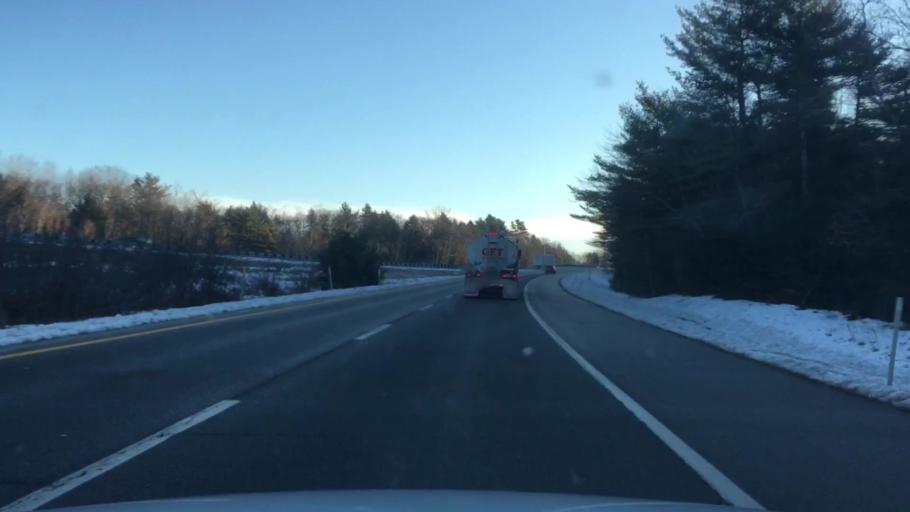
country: US
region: Maine
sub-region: Sagadahoc County
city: Topsham
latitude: 43.9171
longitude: -70.0196
